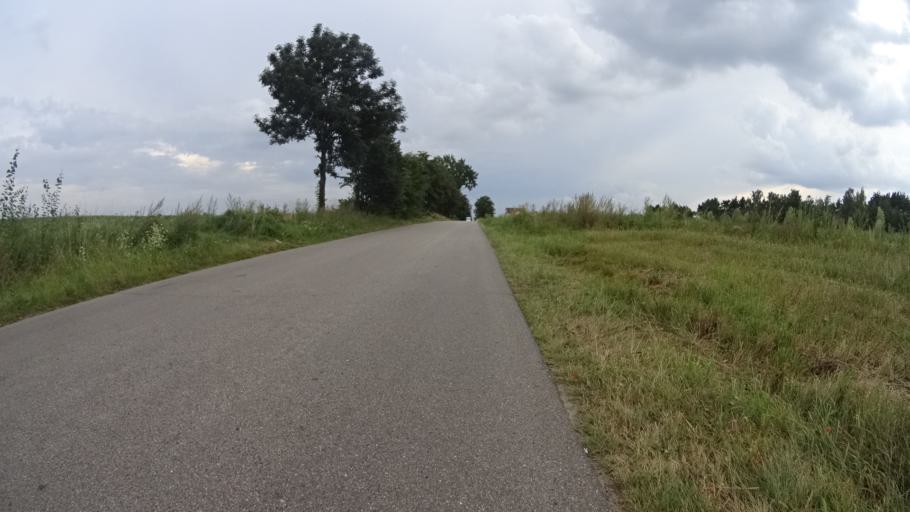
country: PL
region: Masovian Voivodeship
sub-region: Powiat bialobrzeski
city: Wysmierzyce
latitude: 51.6694
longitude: 20.8567
